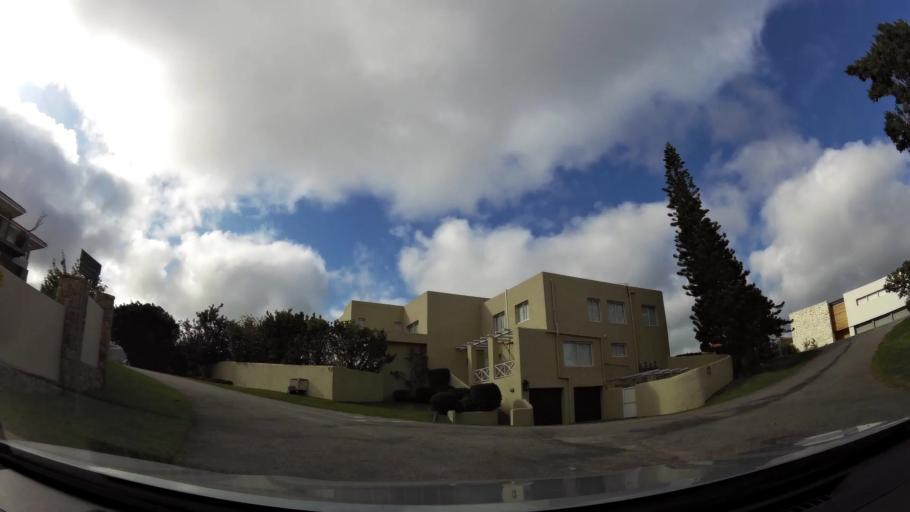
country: ZA
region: Western Cape
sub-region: Eden District Municipality
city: Plettenberg Bay
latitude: -34.0723
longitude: 23.3717
